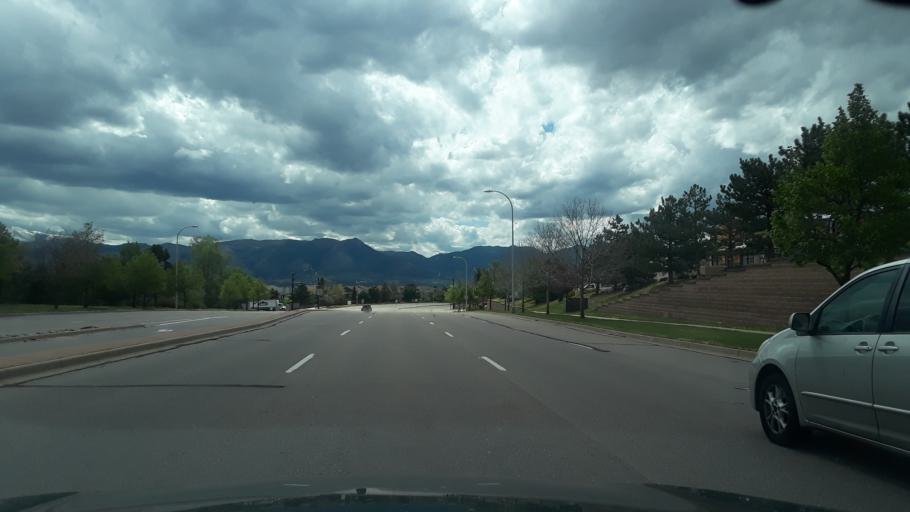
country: US
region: Colorado
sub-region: El Paso County
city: Black Forest
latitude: 38.9569
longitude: -104.7671
